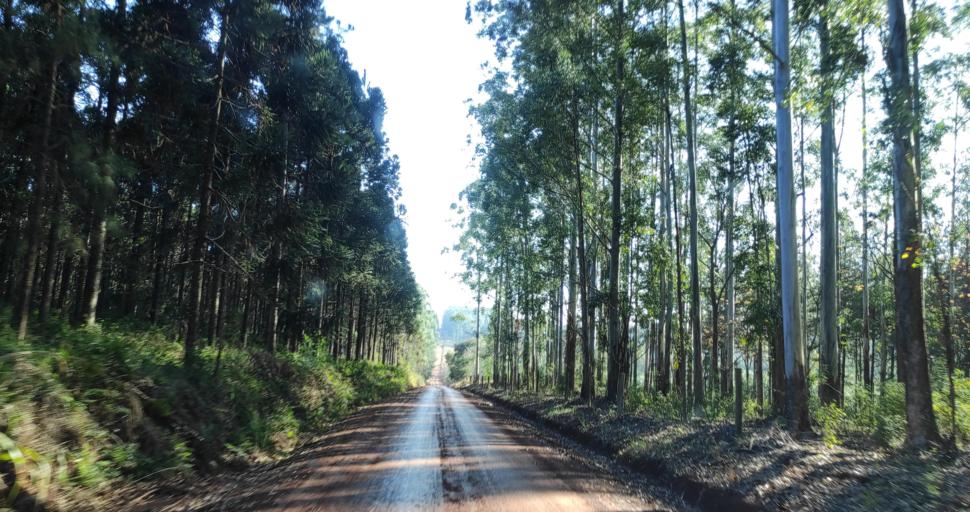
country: AR
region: Misiones
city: Capiovi
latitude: -26.8734
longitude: -55.0160
